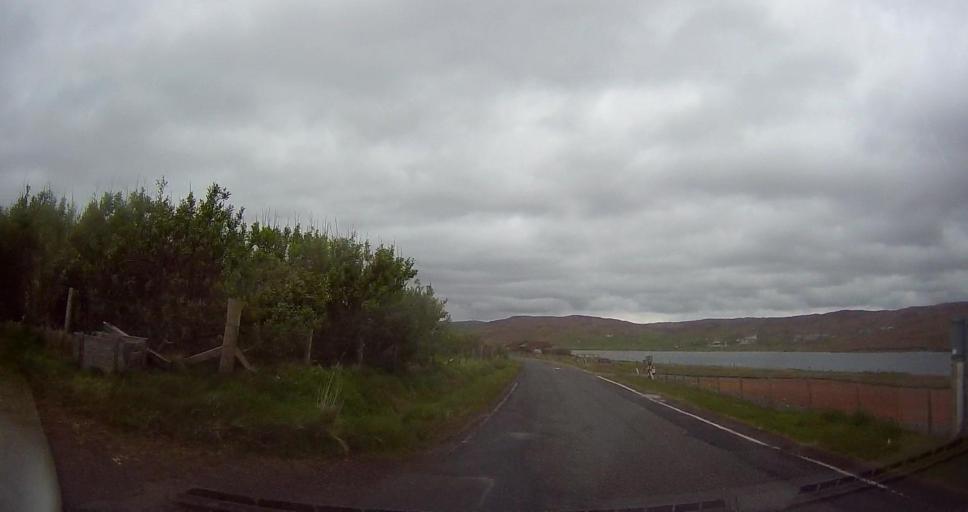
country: GB
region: Scotland
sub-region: Shetland Islands
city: Lerwick
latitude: 60.4839
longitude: -1.4718
